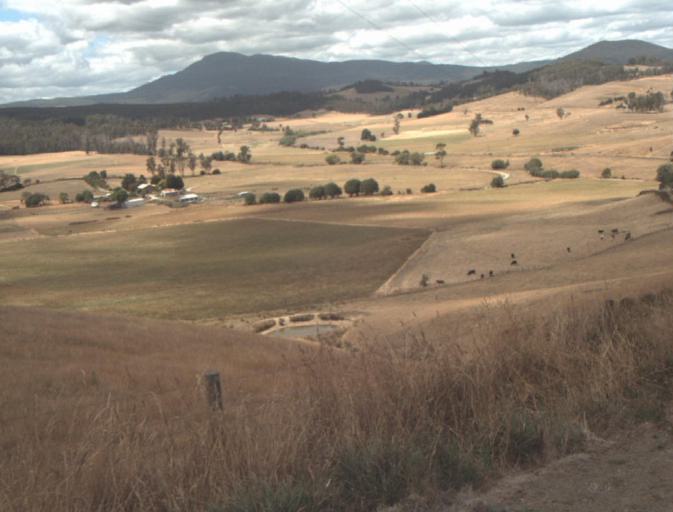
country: AU
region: Tasmania
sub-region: Launceston
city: Mayfield
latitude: -41.2073
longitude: 147.1395
